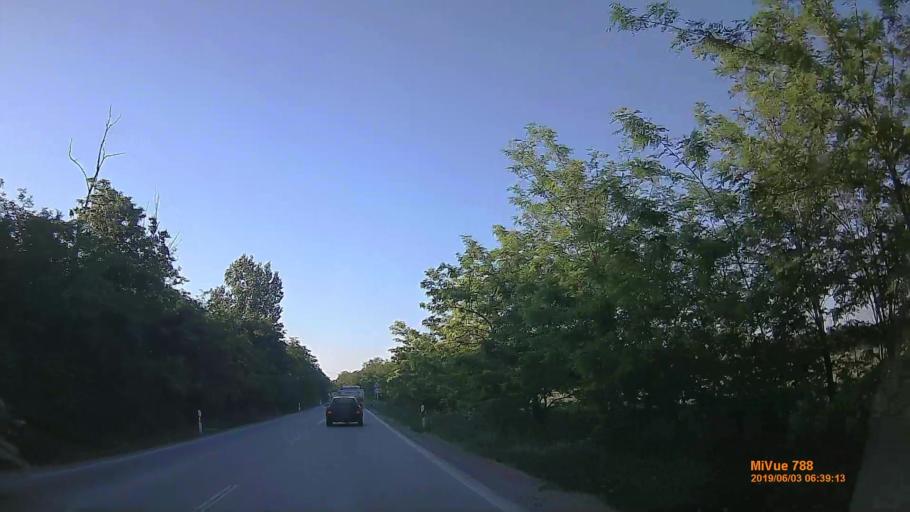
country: HU
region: Pest
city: Dunavarsany
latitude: 47.2889
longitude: 19.0983
